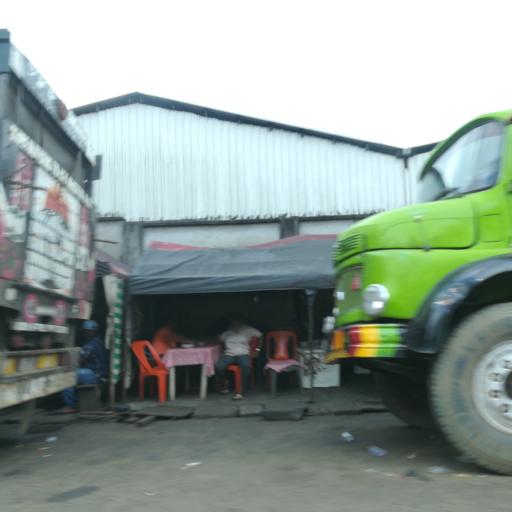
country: NG
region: Rivers
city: Port Harcourt
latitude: 4.8112
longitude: 7.0381
